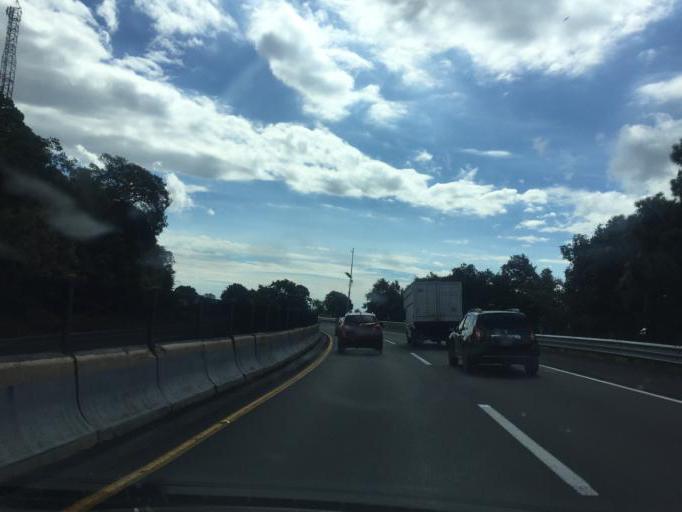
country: MX
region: Morelos
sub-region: Cuernavaca
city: Villa Santiago
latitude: 19.0252
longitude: -99.1966
